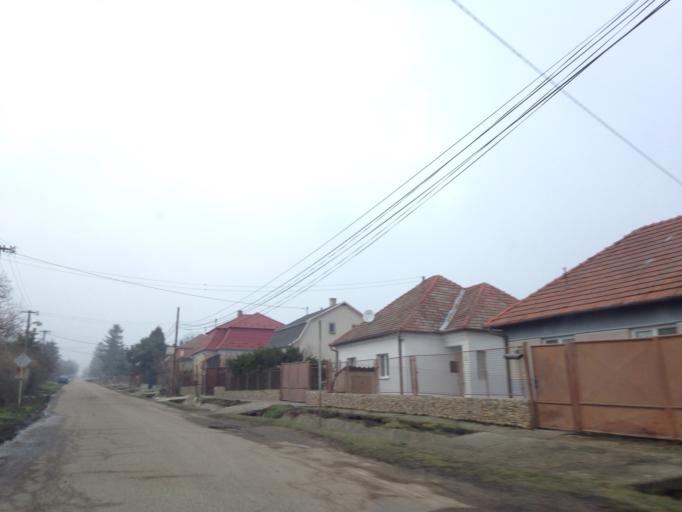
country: SK
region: Nitriansky
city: Svodin
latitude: 47.9920
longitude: 18.3917
